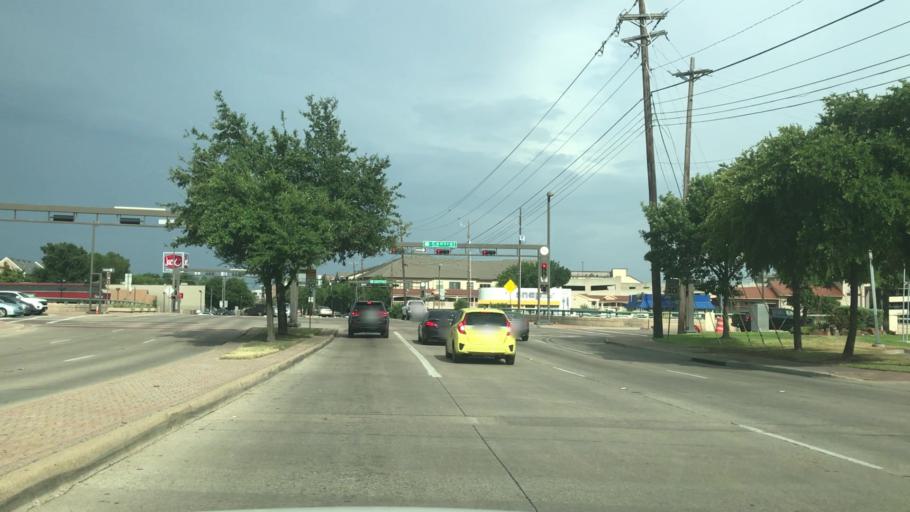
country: US
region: Texas
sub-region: Dallas County
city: Highland Park
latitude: 32.8159
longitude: -96.7905
